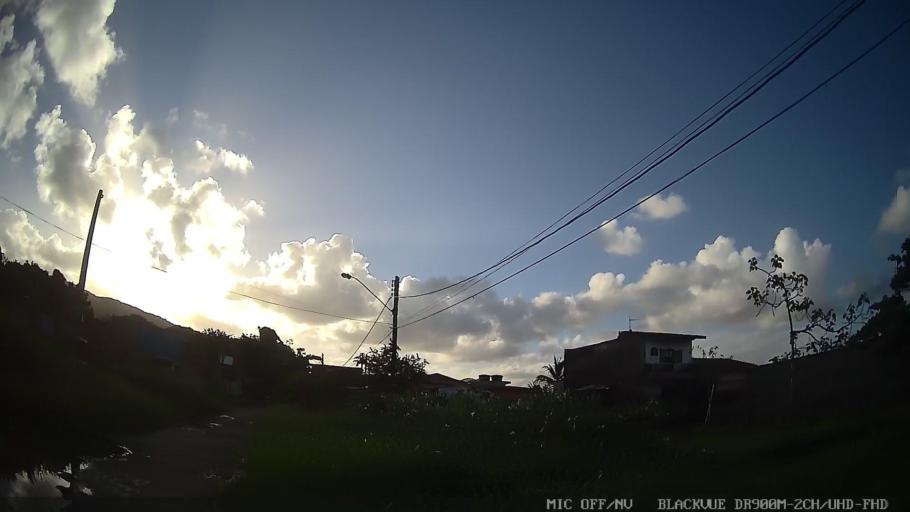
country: BR
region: Sao Paulo
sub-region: Itanhaem
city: Itanhaem
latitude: -24.1375
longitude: -46.7188
